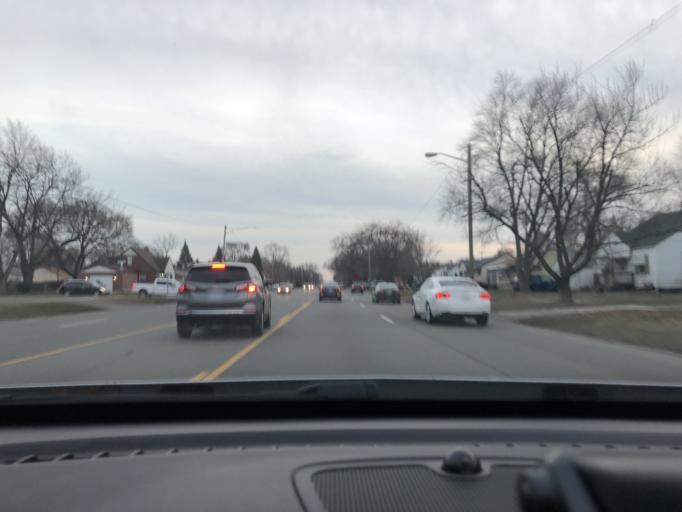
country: US
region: Michigan
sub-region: Wayne County
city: Allen Park
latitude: 42.2546
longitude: -83.2312
